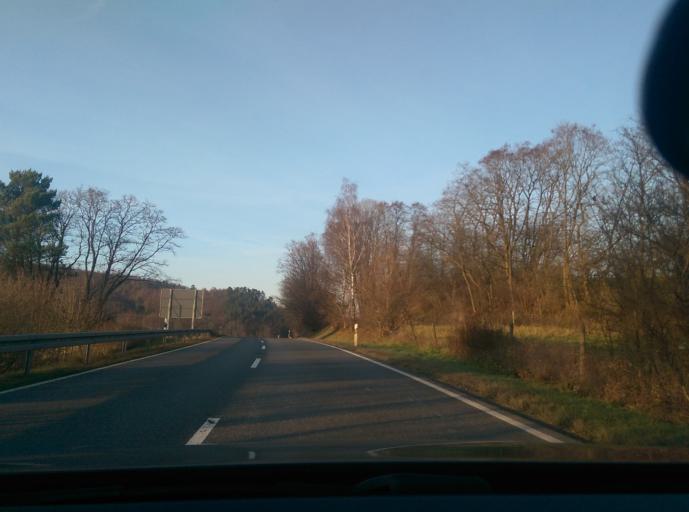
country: DE
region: Hesse
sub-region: Regierungsbezirk Kassel
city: Nentershausen
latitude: 51.0322
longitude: 10.0100
